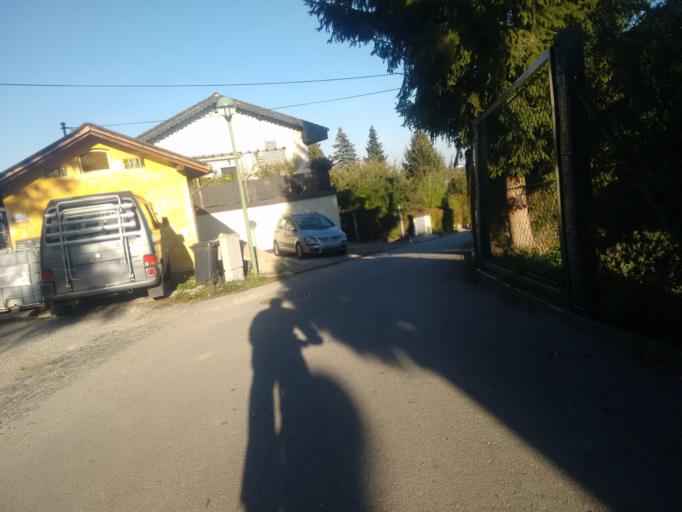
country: AT
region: Upper Austria
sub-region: Wels Stadt
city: Wels
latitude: 48.1837
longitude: 13.9896
